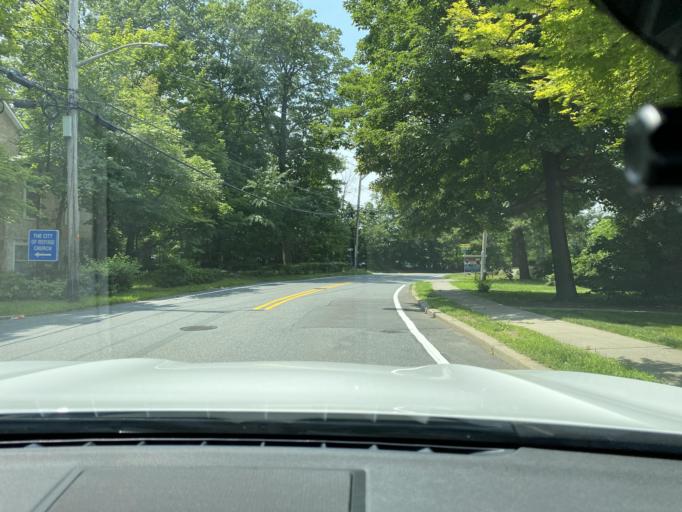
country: US
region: New York
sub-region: Rockland County
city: Suffern
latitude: 41.1005
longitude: -74.1560
